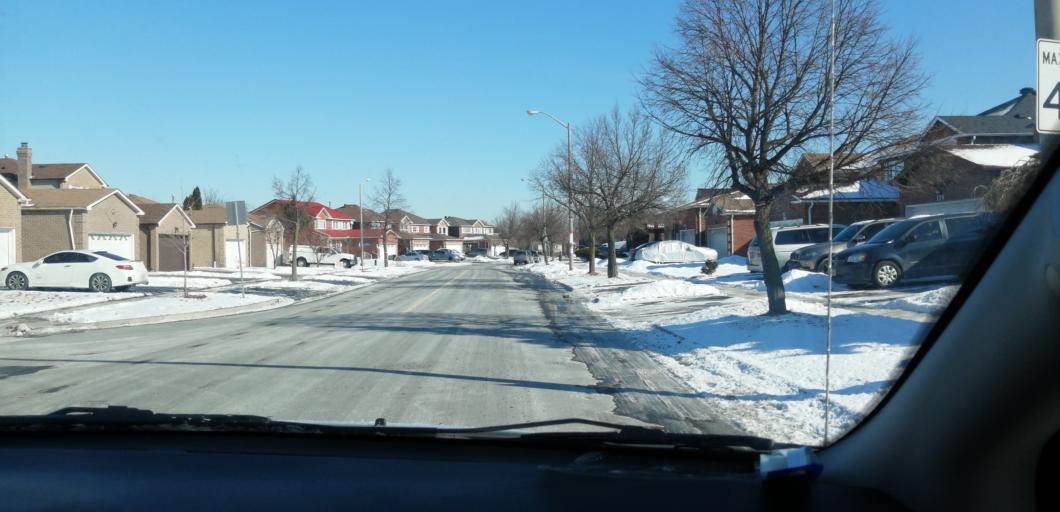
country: CA
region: Ontario
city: Scarborough
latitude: 43.8160
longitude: -79.2174
